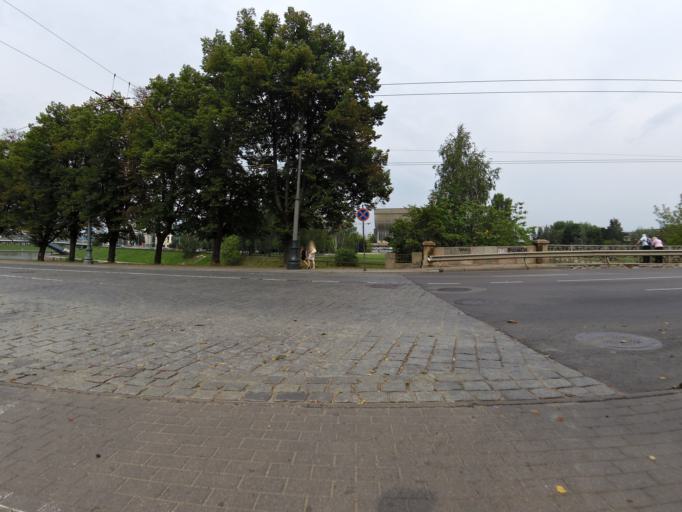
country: LT
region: Vilnius County
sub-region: Vilnius
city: Vilnius
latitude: 54.6885
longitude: 25.2924
